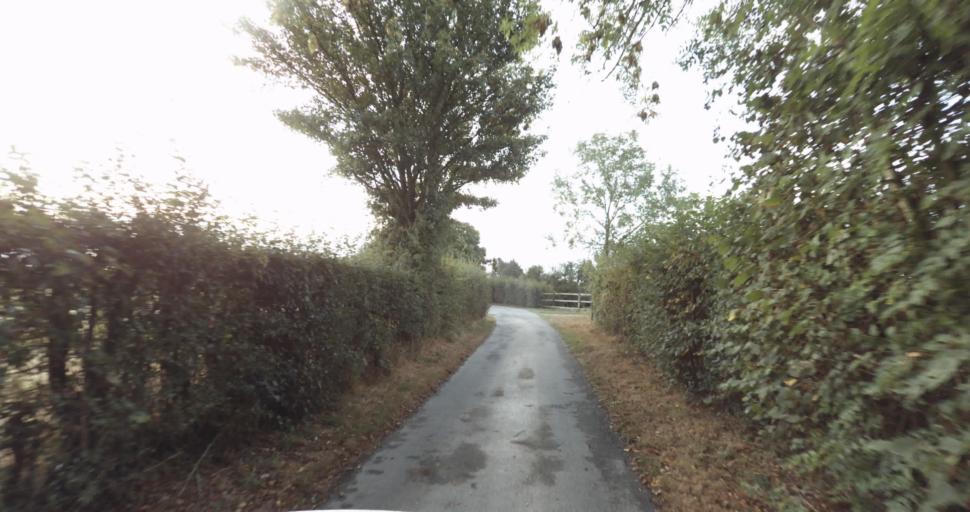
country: FR
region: Lower Normandy
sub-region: Departement de l'Orne
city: Vimoutiers
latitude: 48.9354
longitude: 0.2155
